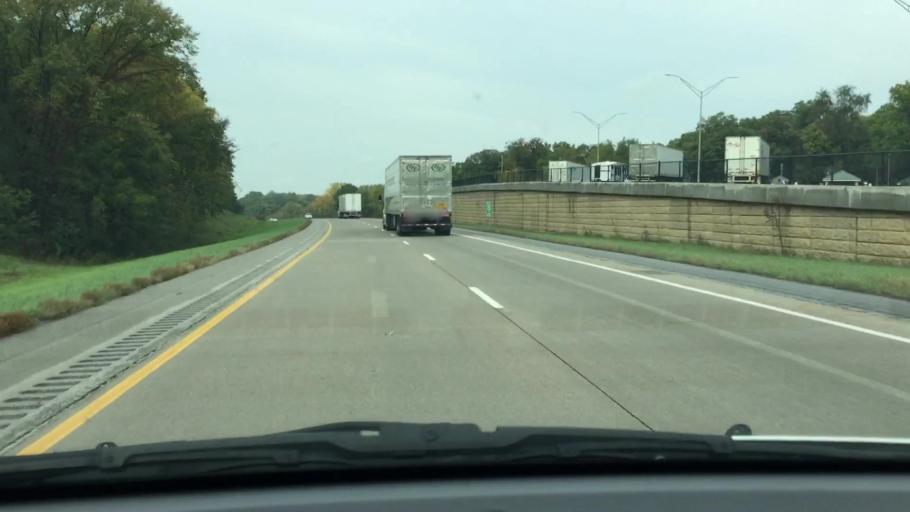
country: US
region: Iowa
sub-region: Muscatine County
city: Wilton
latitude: 41.6412
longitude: -91.0534
